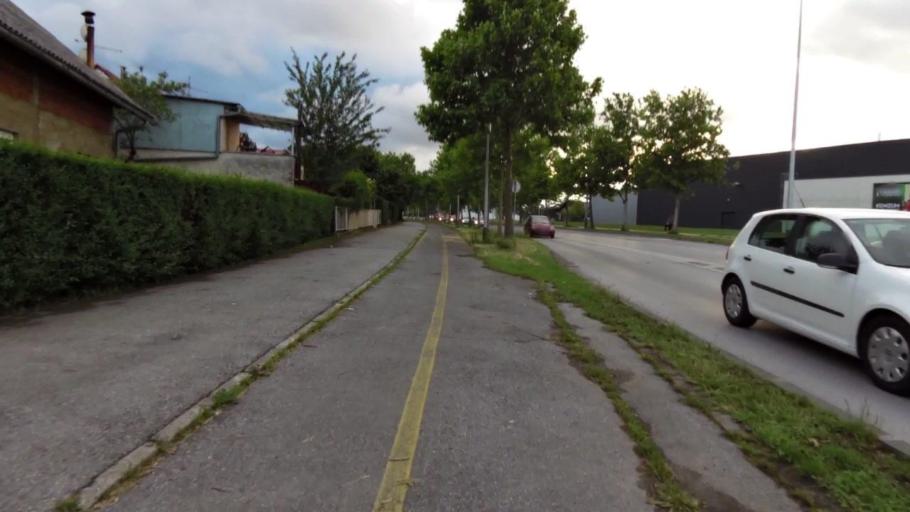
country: HR
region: Grad Zagreb
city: Dubrava
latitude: 45.8410
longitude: 16.0551
